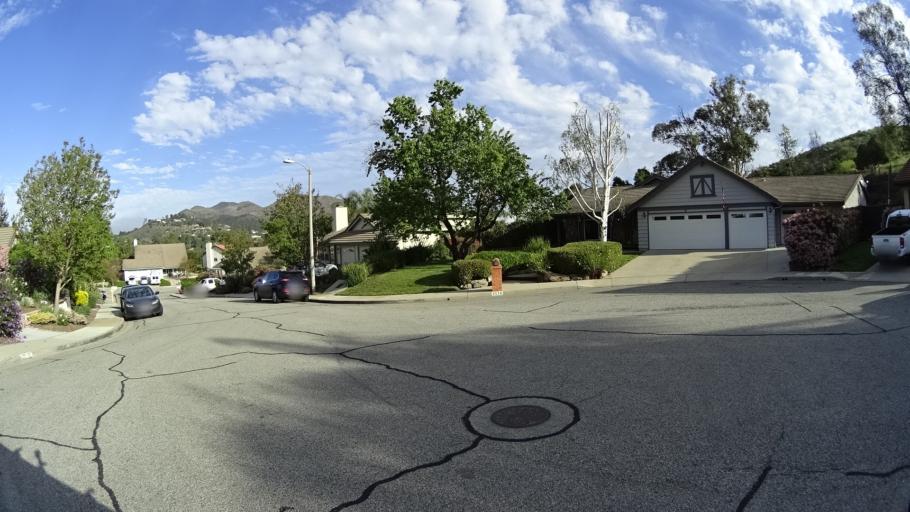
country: US
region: California
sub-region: Ventura County
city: Casa Conejo
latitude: 34.1700
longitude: -118.9521
